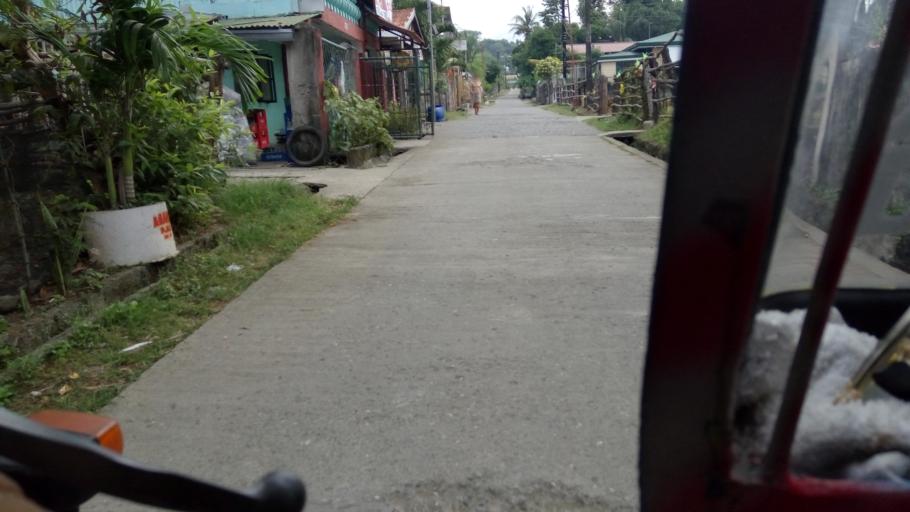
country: PH
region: Ilocos
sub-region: Province of La Union
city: Payocpoc Sur
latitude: 16.5038
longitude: 120.3317
